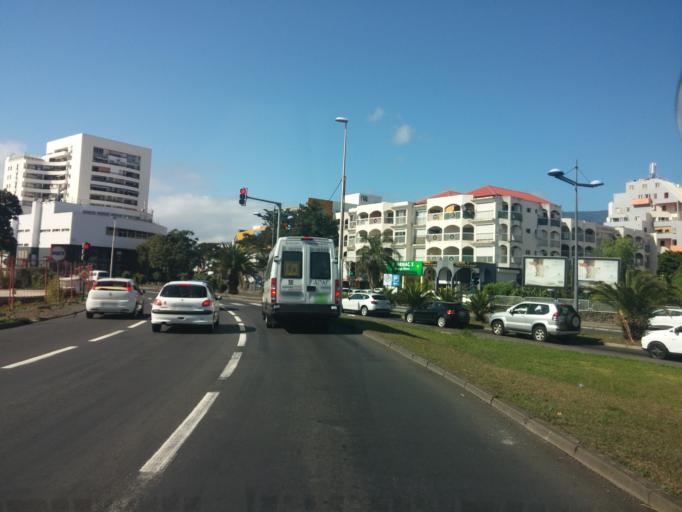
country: RE
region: Reunion
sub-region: Reunion
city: Saint-Denis
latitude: -20.8851
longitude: 55.4678
